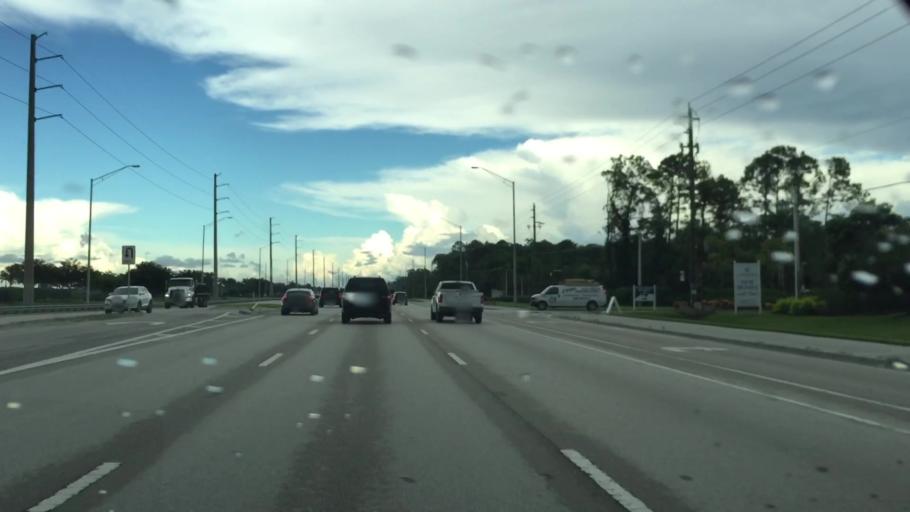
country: US
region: Florida
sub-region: Collier County
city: Vineyards
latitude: 26.2731
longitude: -81.6701
